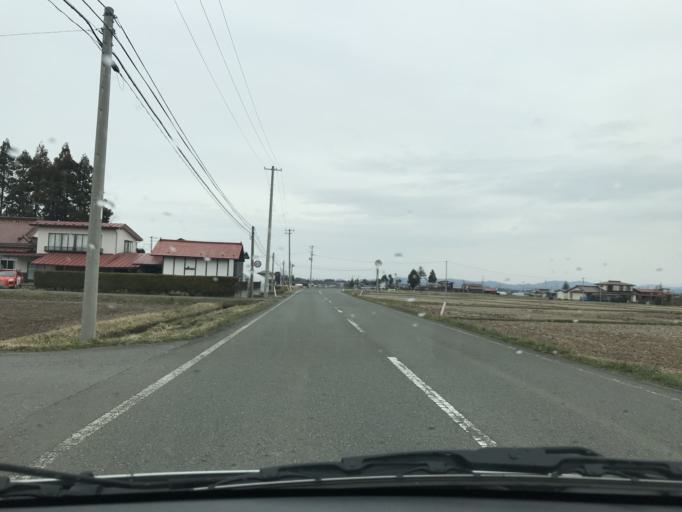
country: JP
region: Iwate
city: Mizusawa
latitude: 39.1695
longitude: 141.1112
